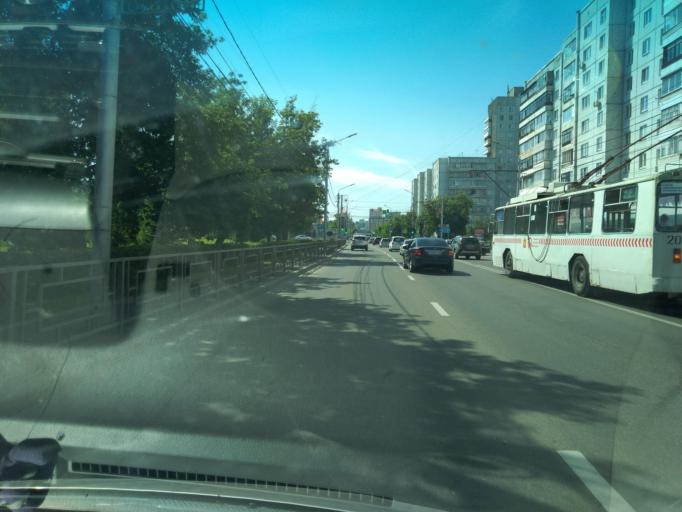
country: RU
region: Krasnoyarskiy
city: Krasnoyarsk
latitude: 56.0125
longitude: 92.8154
